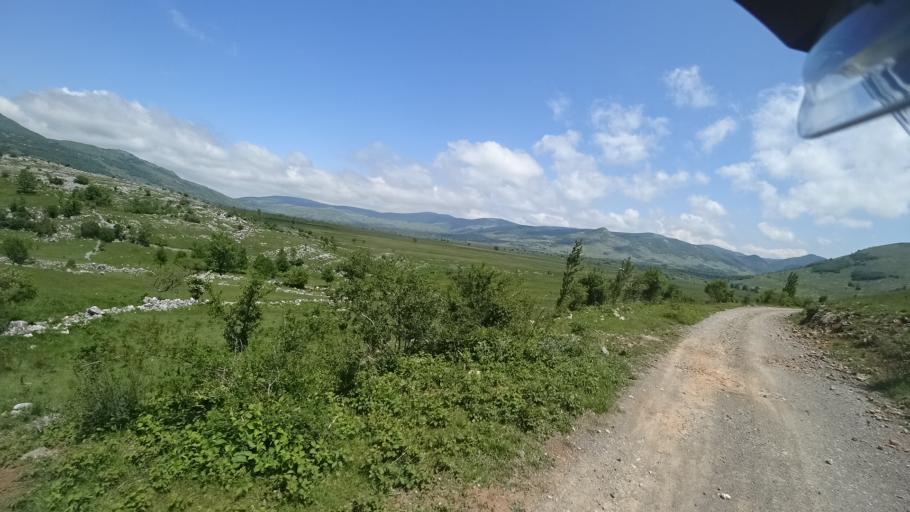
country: HR
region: Zadarska
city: Gracac
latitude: 44.4386
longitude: 15.9203
